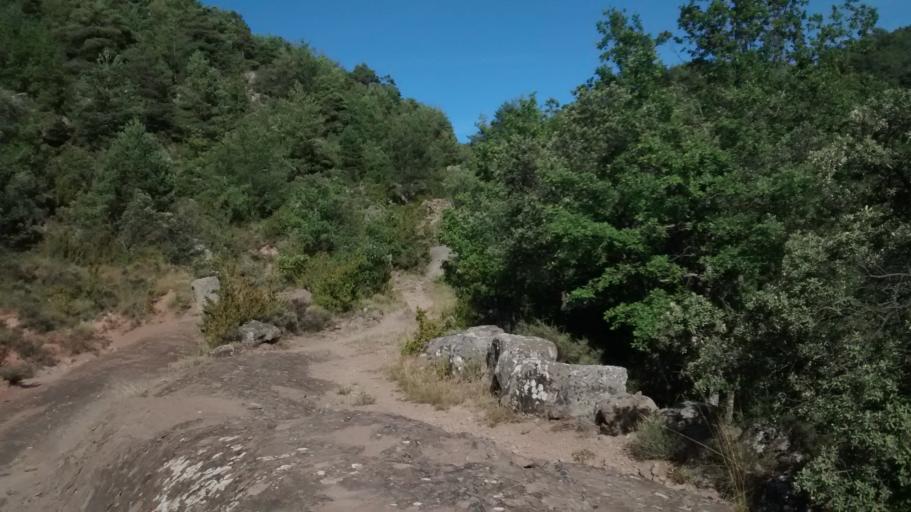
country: ES
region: Aragon
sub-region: Provincia de Huesca
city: Ibieca
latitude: 42.3208
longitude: -0.2444
